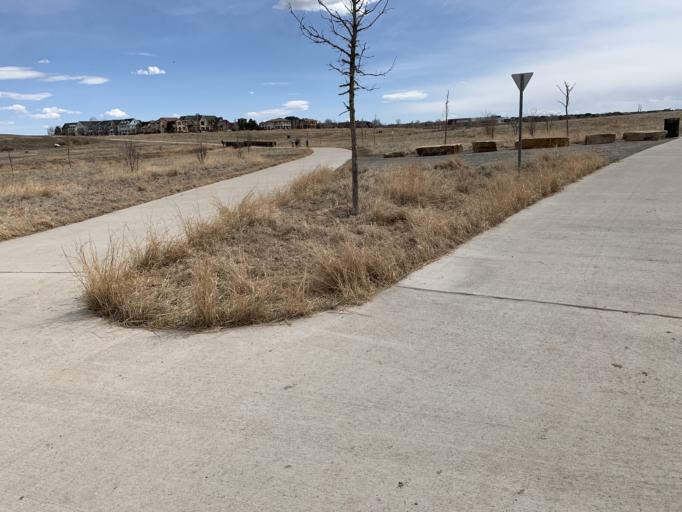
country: US
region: Colorado
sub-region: Adams County
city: Aurora
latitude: 39.7671
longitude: -104.8775
